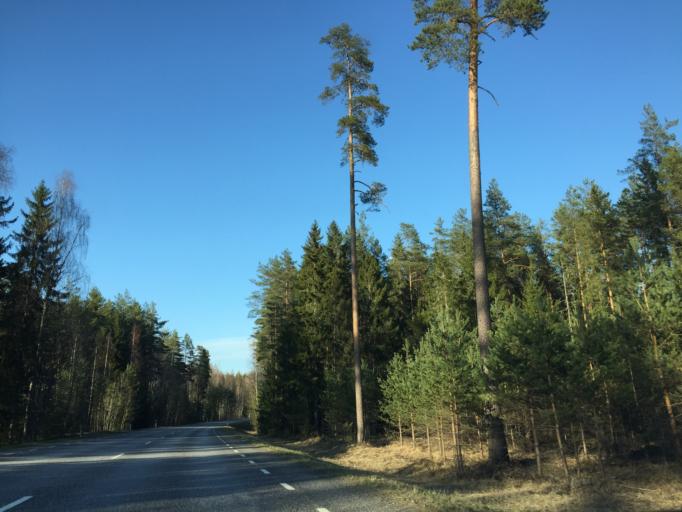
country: EE
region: Valgamaa
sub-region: Torva linn
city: Torva
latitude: 58.1241
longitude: 26.1371
